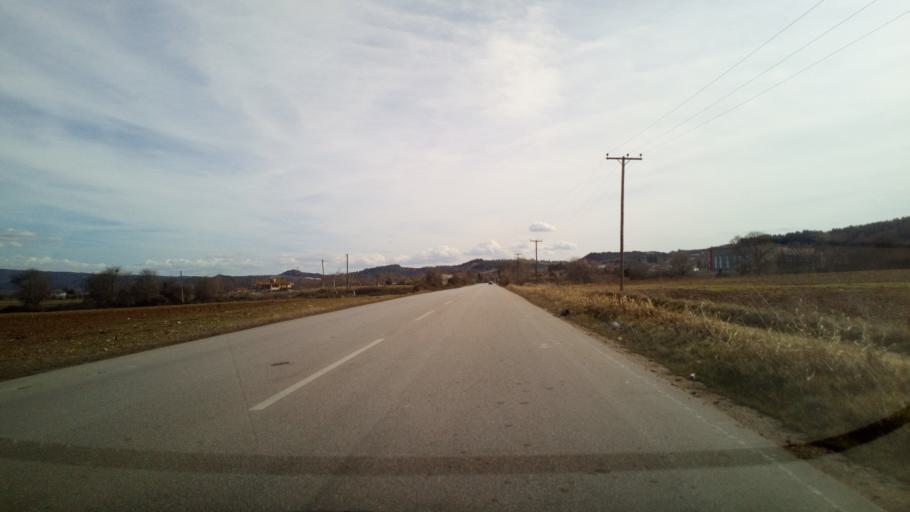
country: GR
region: Central Macedonia
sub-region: Nomos Thessalonikis
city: Gerakarou
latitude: 40.6411
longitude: 23.1839
